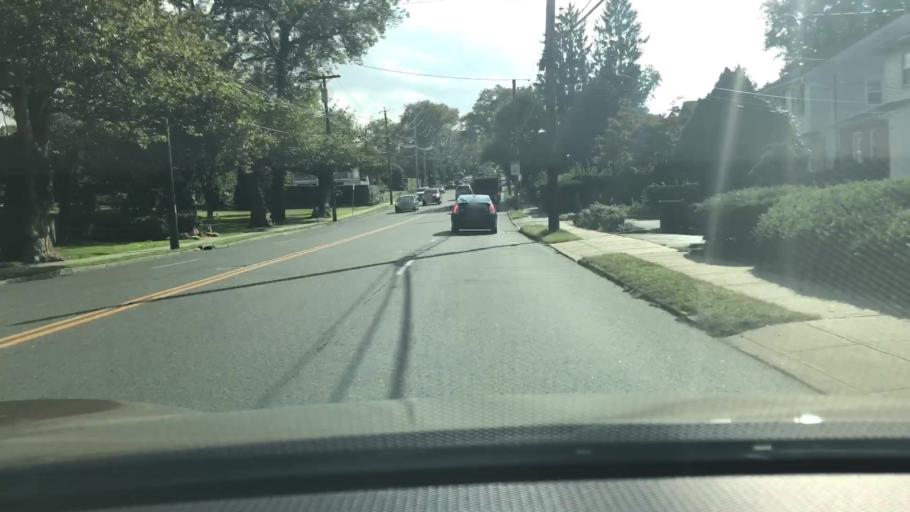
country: US
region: New York
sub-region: Westchester County
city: Tuckahoe
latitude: 40.9653
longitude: -73.8093
